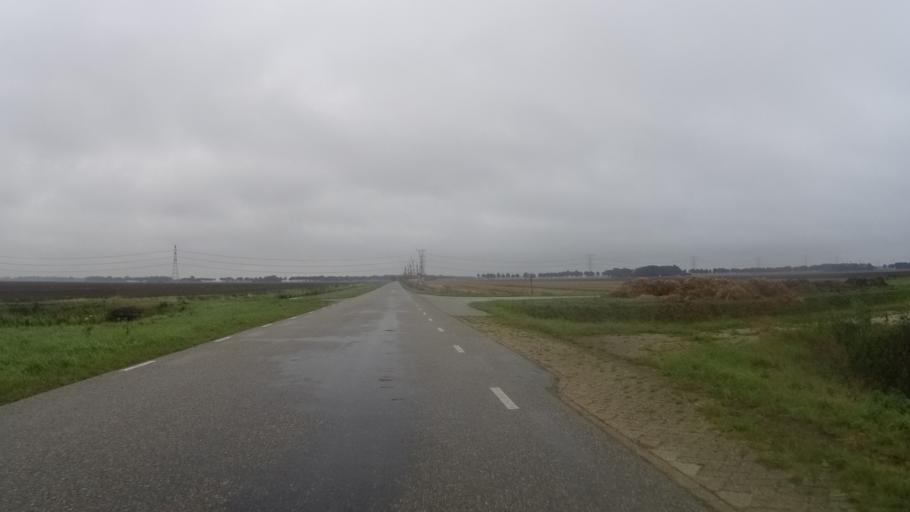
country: NL
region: Groningen
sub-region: Gemeente Veendam
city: Veendam
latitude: 53.1919
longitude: 6.9020
